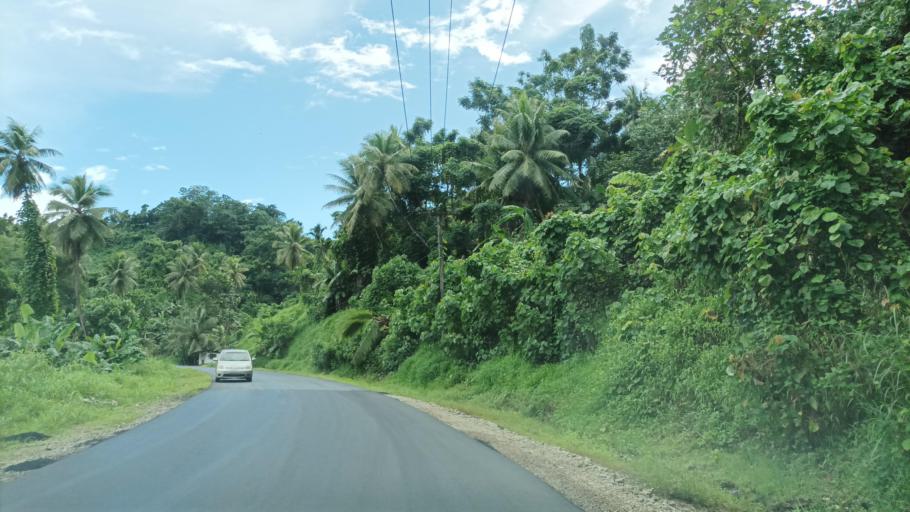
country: FM
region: Pohnpei
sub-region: Madolenihm Municipality
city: Madolenihm Municipality Government
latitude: 6.9163
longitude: 158.3049
